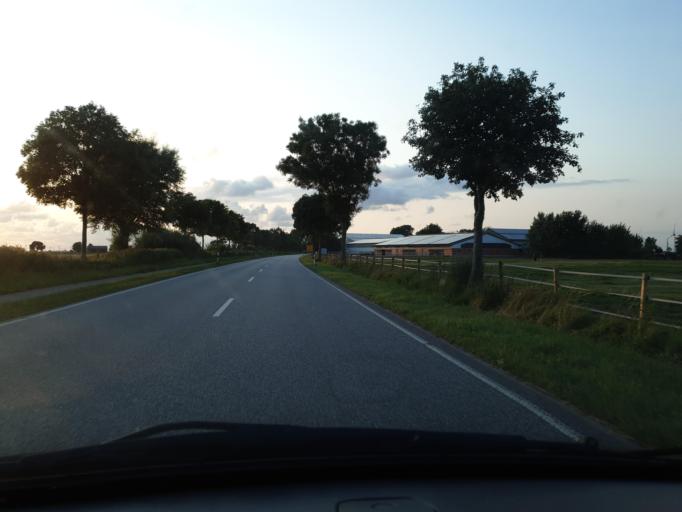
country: DE
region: Schleswig-Holstein
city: Schmedeswurth
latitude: 53.9139
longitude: 9.0517
